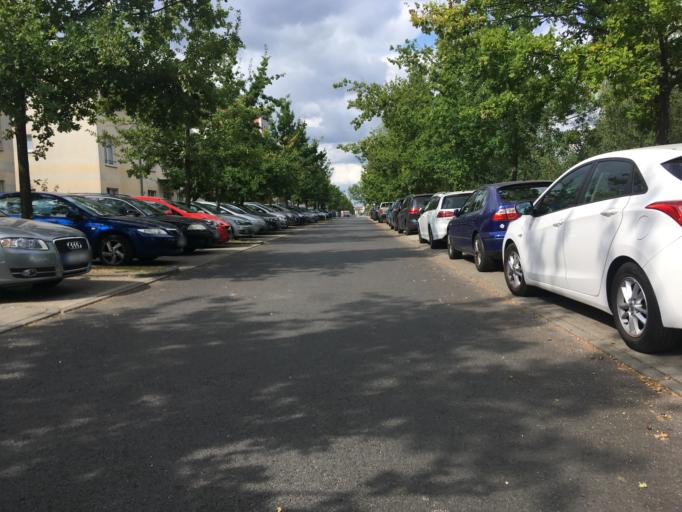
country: DE
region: Berlin
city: Karow
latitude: 52.6138
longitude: 13.4978
